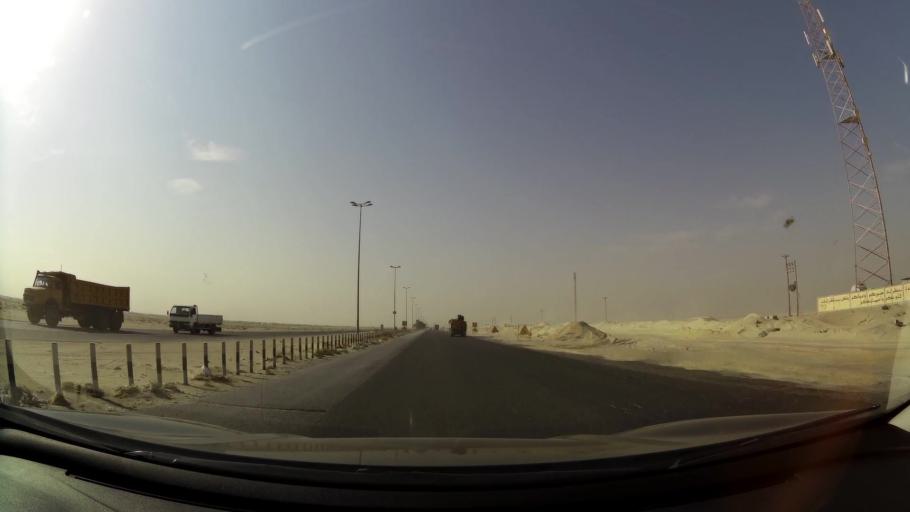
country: KW
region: Al Ahmadi
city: Al Ahmadi
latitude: 28.9052
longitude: 48.0934
